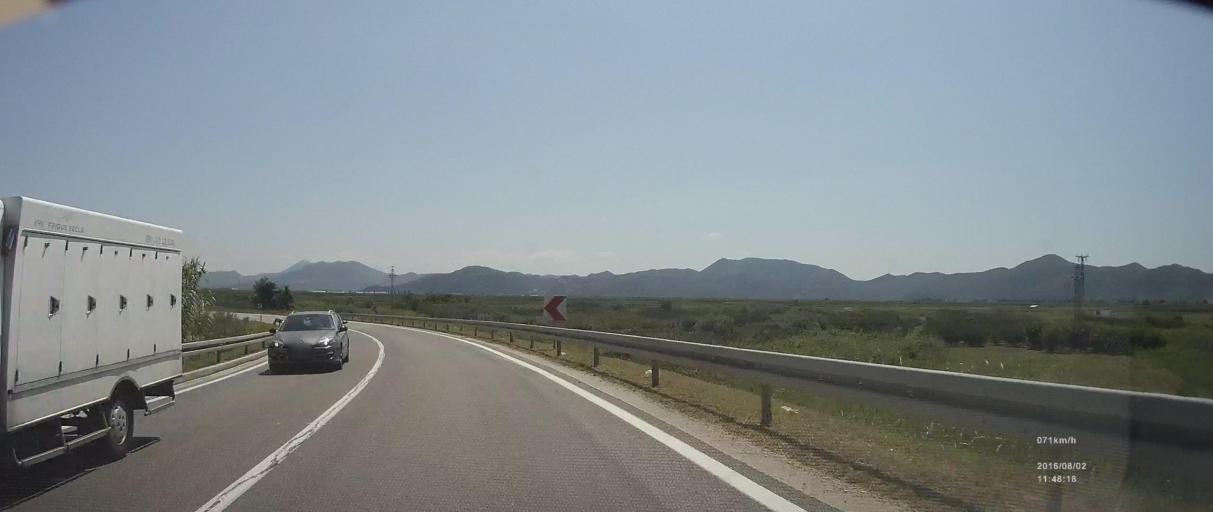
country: HR
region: Dubrovacko-Neretvanska
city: Komin
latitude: 43.0349
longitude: 17.4872
